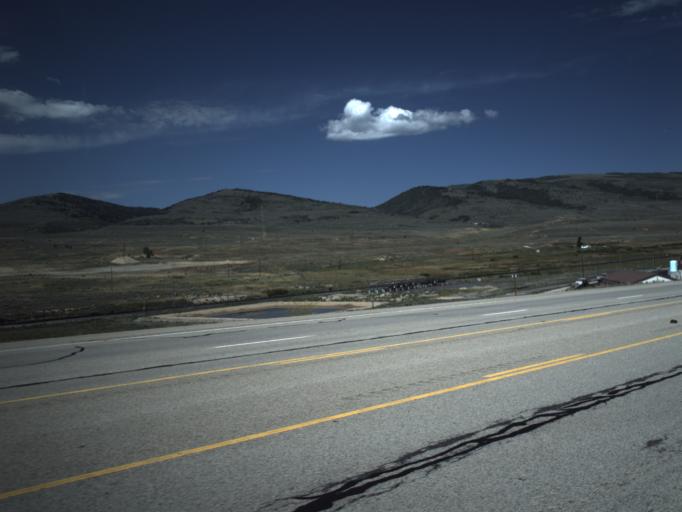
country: US
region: Utah
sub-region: Carbon County
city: Helper
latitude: 39.8505
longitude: -111.0101
